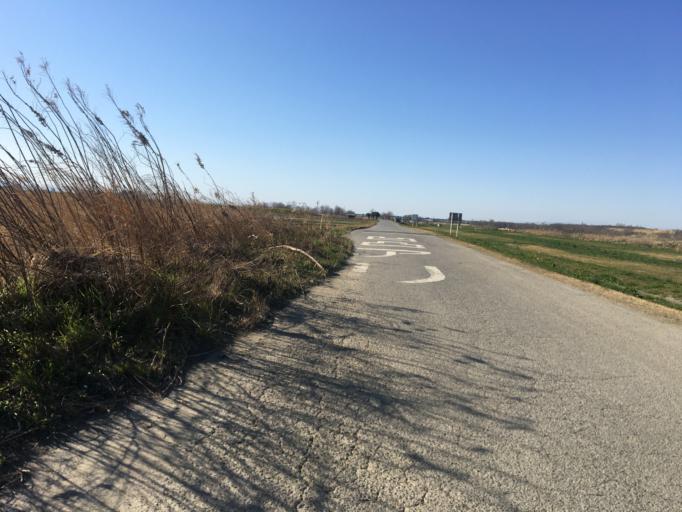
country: JP
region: Saitama
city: Shiki
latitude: 35.8416
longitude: 139.6022
